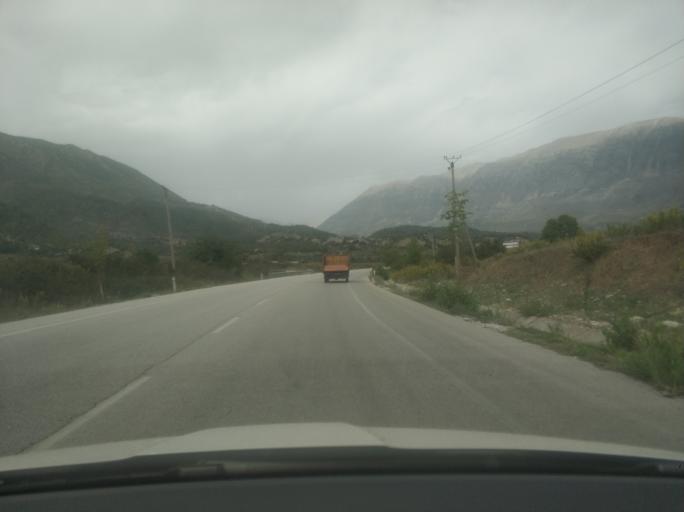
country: AL
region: Gjirokaster
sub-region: Rrethi i Gjirokastres
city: Picar
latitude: 40.1827
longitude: 20.0763
